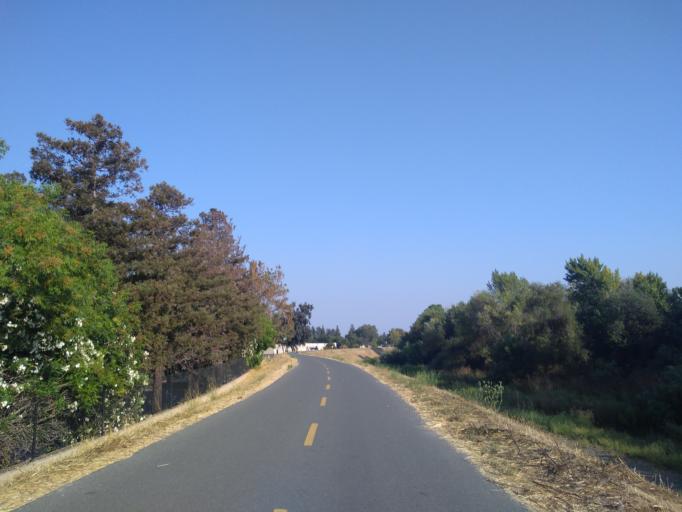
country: US
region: California
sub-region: Santa Clara County
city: Santa Clara
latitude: 37.3893
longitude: -121.9376
